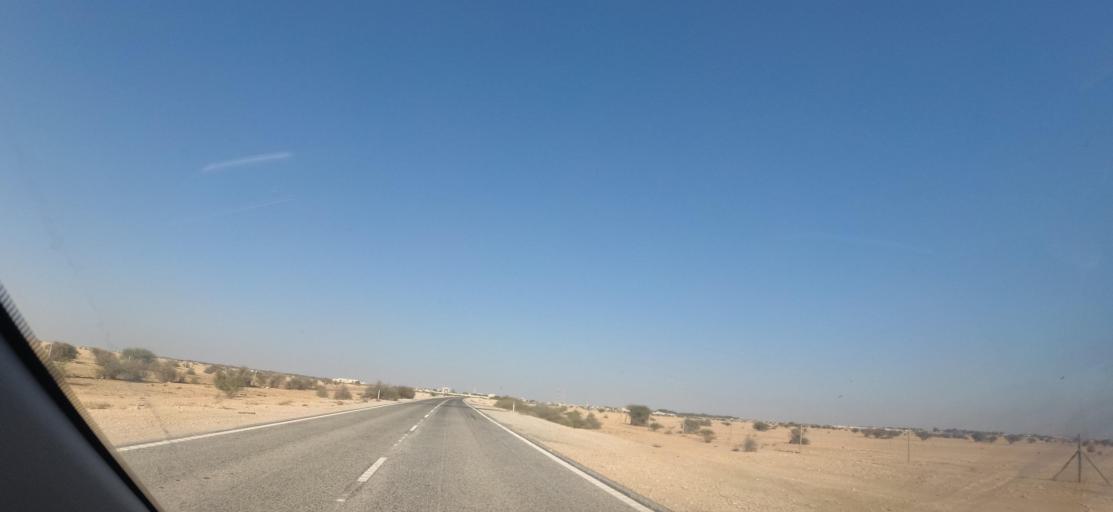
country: QA
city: Al Ghuwayriyah
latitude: 25.8171
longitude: 51.2340
